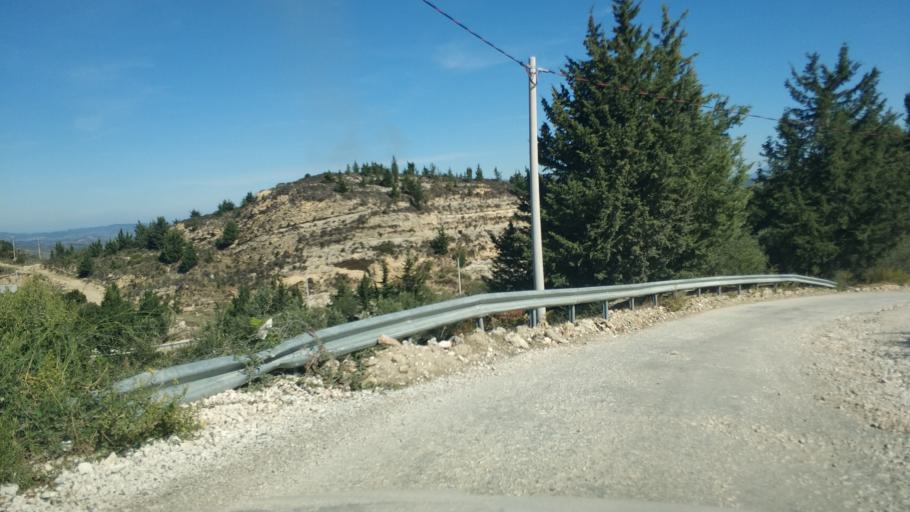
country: AL
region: Vlore
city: Vlore
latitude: 40.4456
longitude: 19.5181
